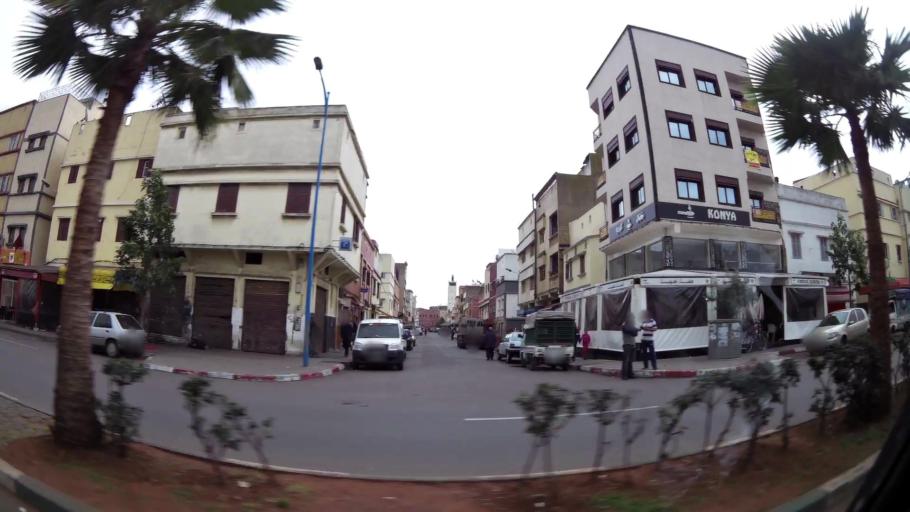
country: MA
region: Grand Casablanca
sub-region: Casablanca
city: Casablanca
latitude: 33.5854
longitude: -7.5573
